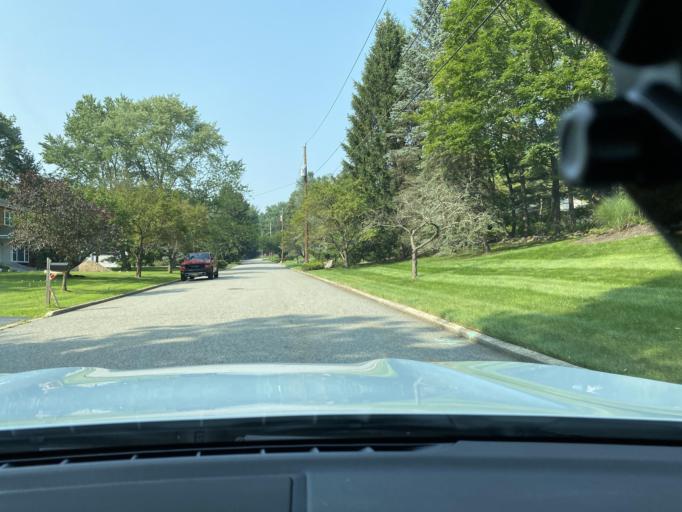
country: US
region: New York
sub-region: Rockland County
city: Airmont
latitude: 41.0796
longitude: -74.1227
